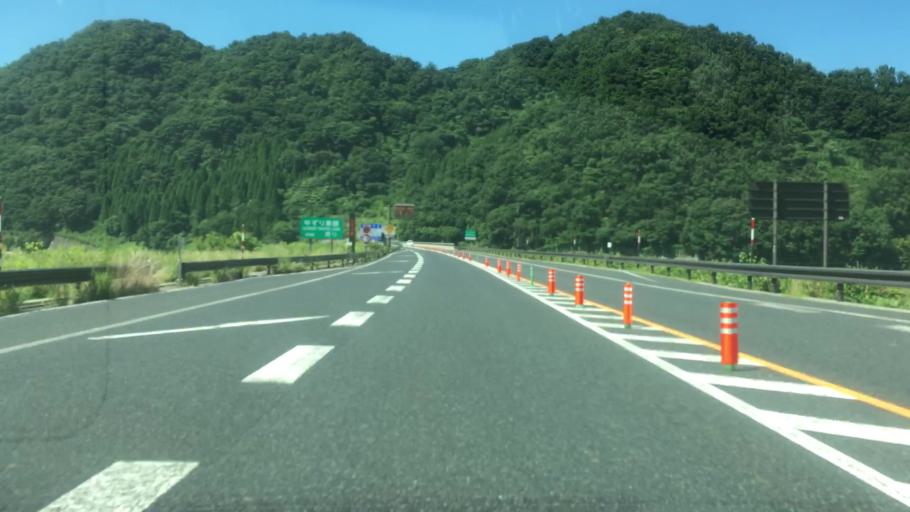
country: JP
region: Tottori
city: Tottori
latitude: 35.3774
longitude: 134.2048
